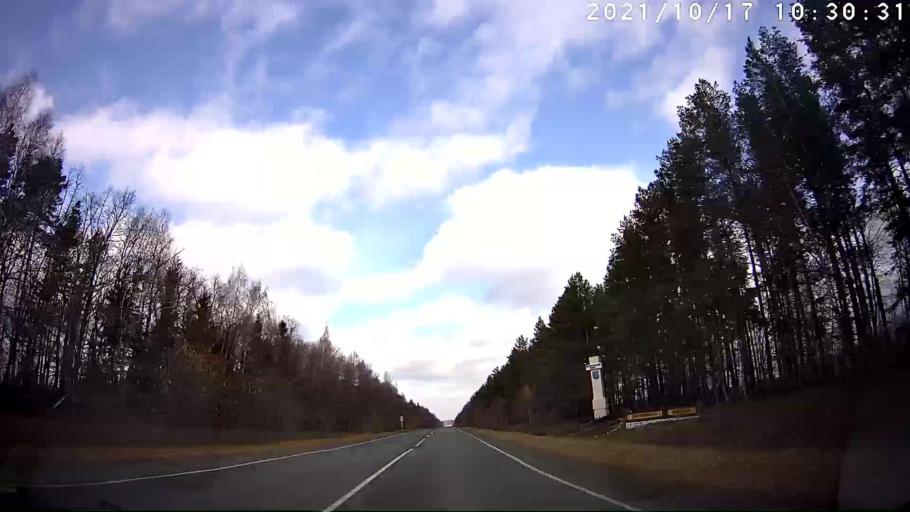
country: RU
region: Mariy-El
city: Kuzhener
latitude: 56.8710
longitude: 48.7549
